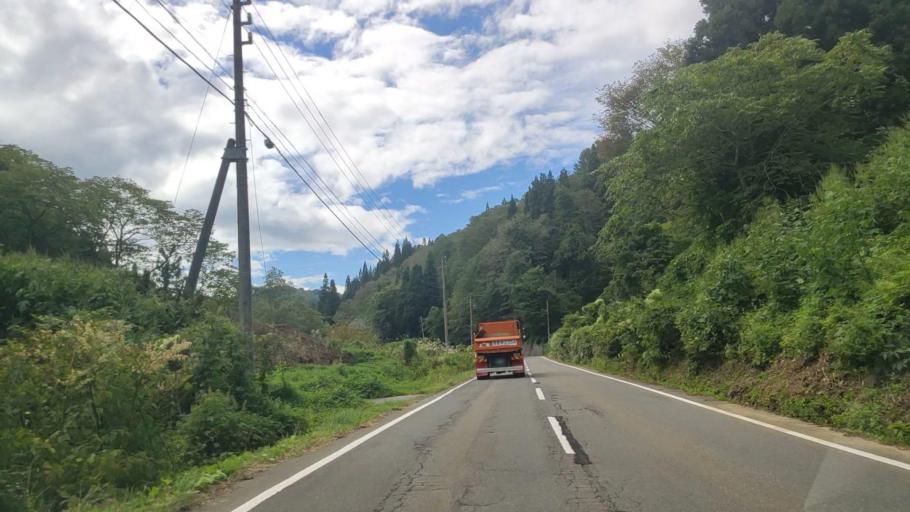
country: JP
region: Nagano
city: Iiyama
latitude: 36.8858
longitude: 138.3224
